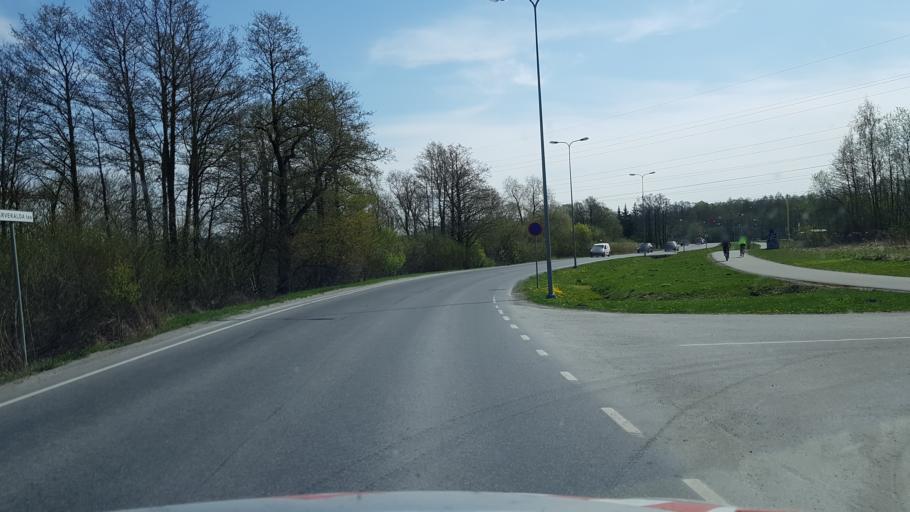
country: EE
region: Harju
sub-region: Saue vald
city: Laagri
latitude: 59.4087
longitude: 24.6161
